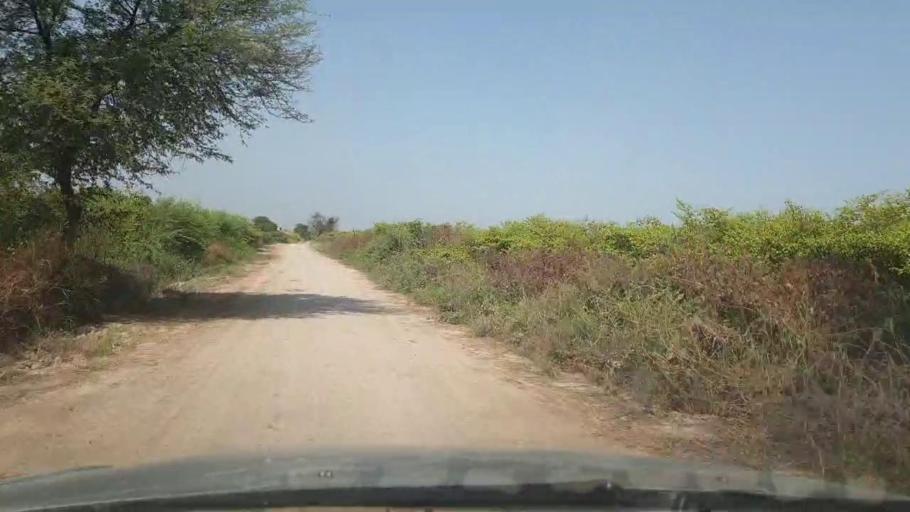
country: PK
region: Sindh
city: Tando Ghulam Ali
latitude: 25.1551
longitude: 68.9089
